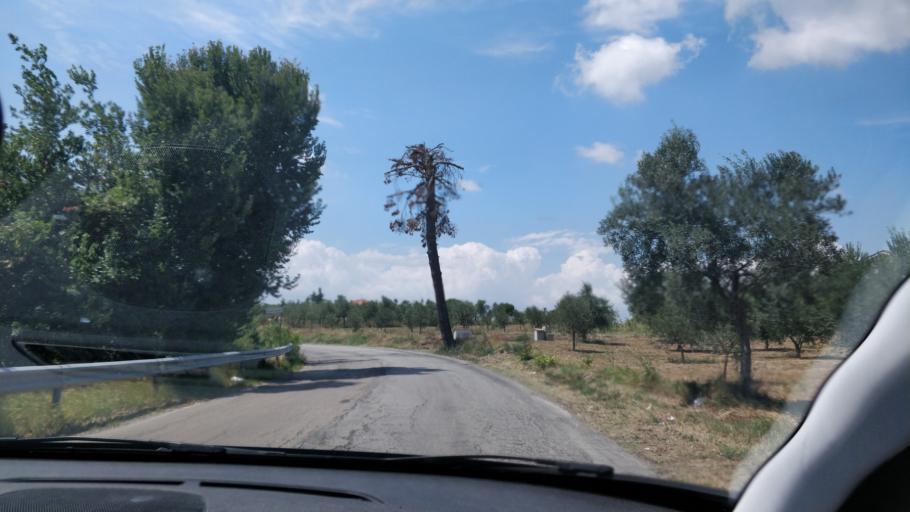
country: IT
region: Abruzzo
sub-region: Provincia di Chieti
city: Torrevecchia
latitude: 42.3981
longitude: 14.2102
